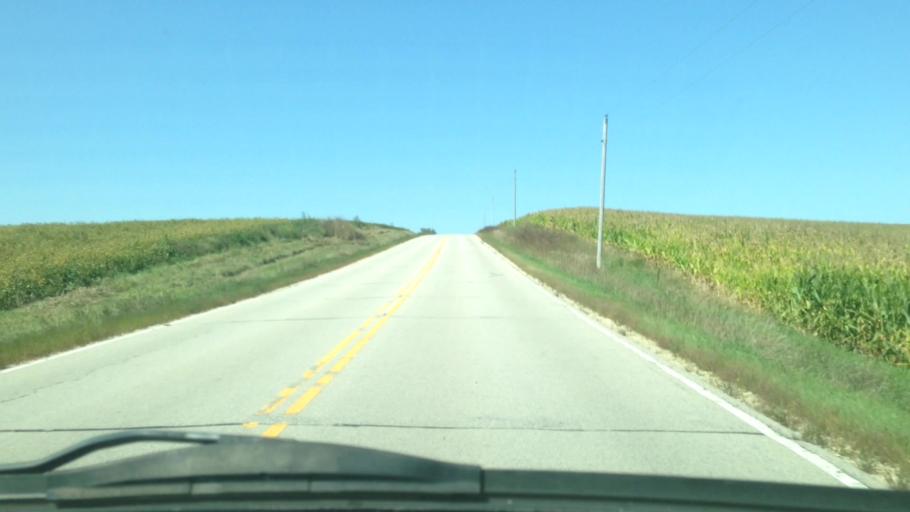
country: US
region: Minnesota
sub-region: Fillmore County
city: Rushford
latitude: 43.7107
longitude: -91.7703
